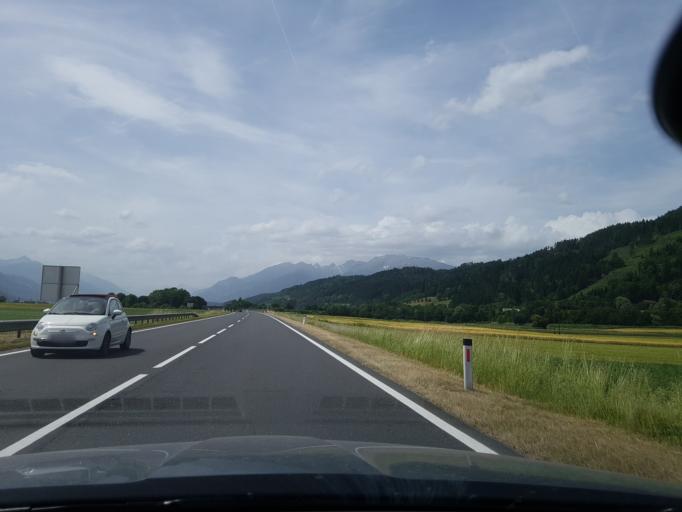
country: AT
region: Carinthia
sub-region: Politischer Bezirk Spittal an der Drau
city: Millstatt
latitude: 46.7756
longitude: 13.5452
